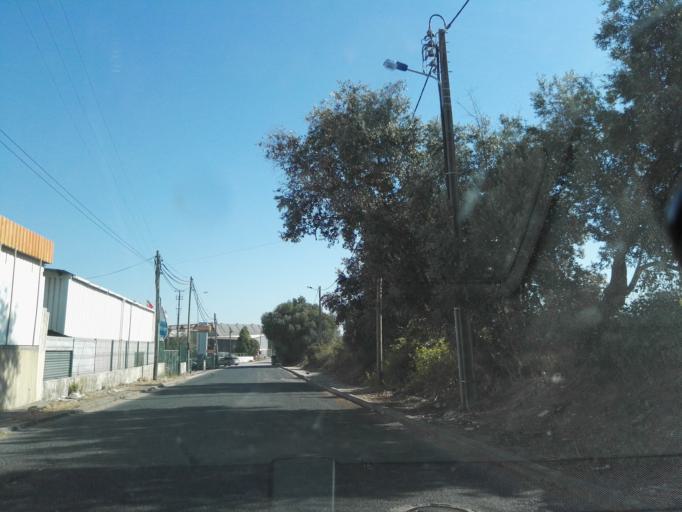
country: PT
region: Lisbon
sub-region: Vila Franca de Xira
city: Sobralinho
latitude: 38.9051
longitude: -9.0259
